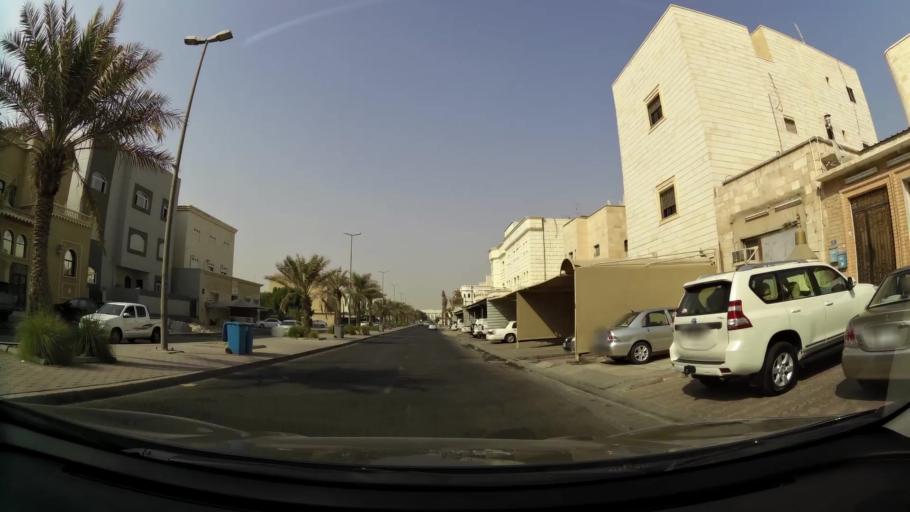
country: KW
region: Al Asimah
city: Ar Rabiyah
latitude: 29.2709
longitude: 47.8802
